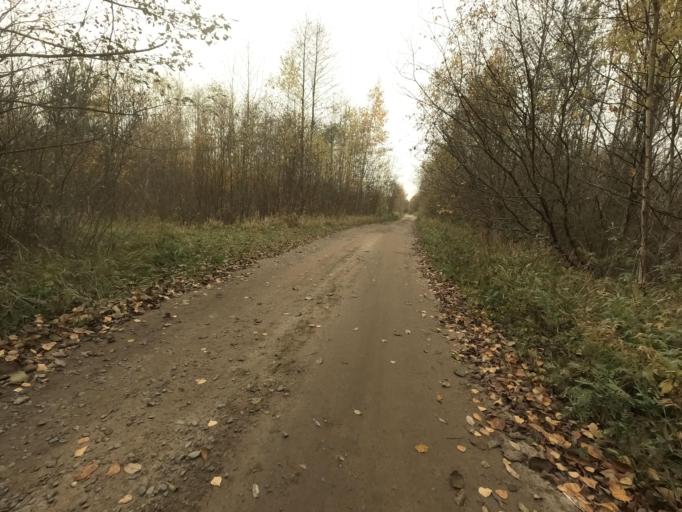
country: RU
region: Leningrad
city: Pavlovo
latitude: 59.7886
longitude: 30.8848
